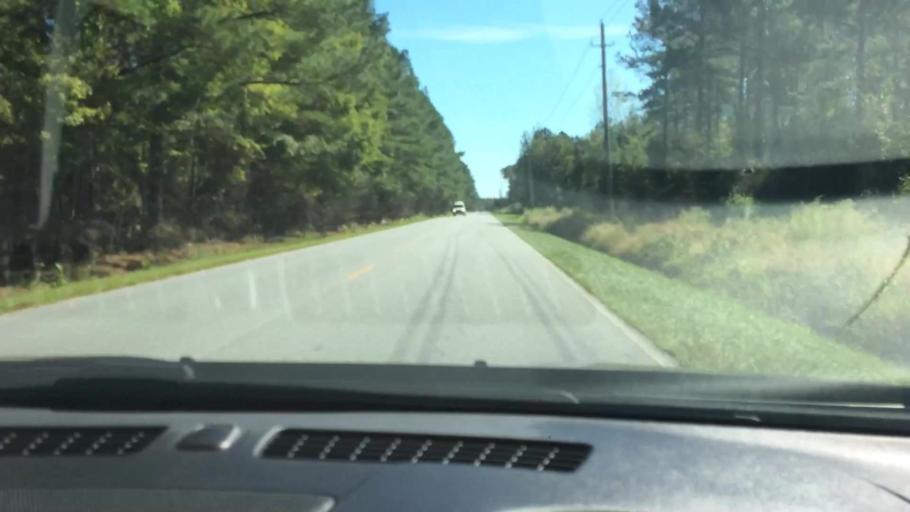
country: US
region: North Carolina
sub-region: Pitt County
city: Grifton
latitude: 35.3990
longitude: -77.4049
